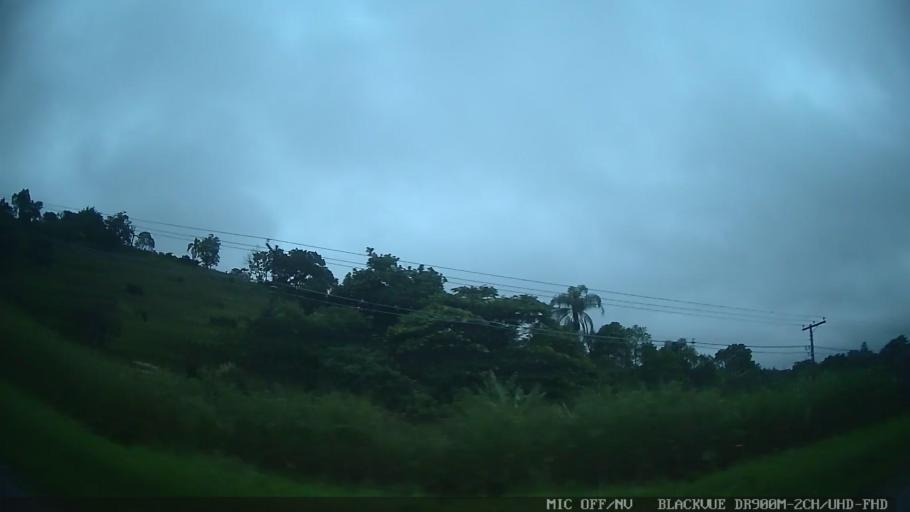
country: BR
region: Sao Paulo
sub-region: Aruja
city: Aruja
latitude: -23.4036
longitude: -46.3077
